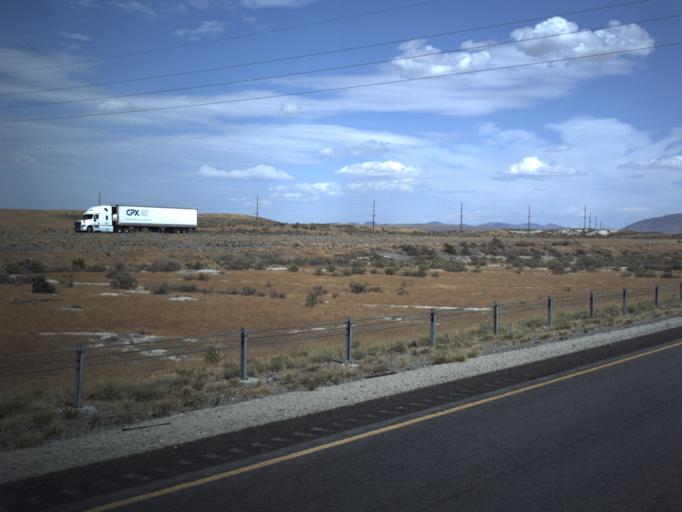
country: US
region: Utah
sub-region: Tooele County
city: Grantsville
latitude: 40.7251
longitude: -113.1436
